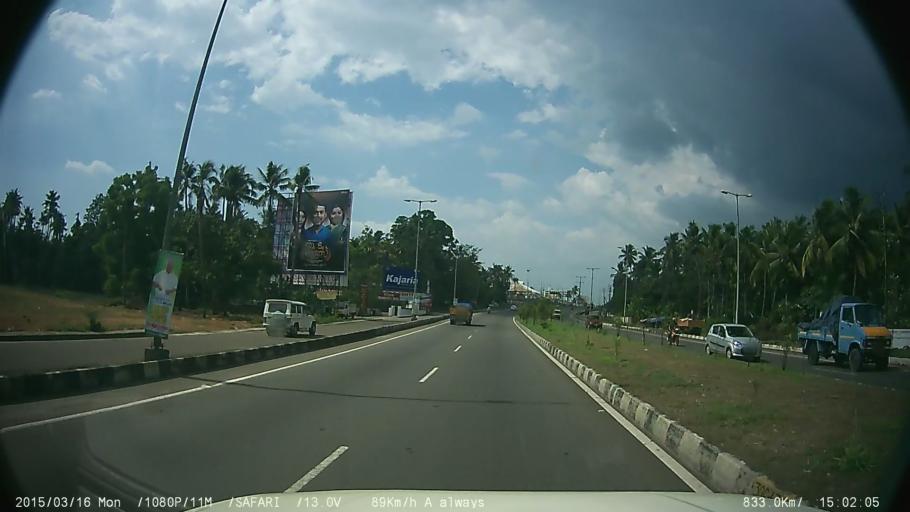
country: IN
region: Kerala
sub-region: Ernakulam
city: Angamali
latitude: 10.2313
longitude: 76.3737
